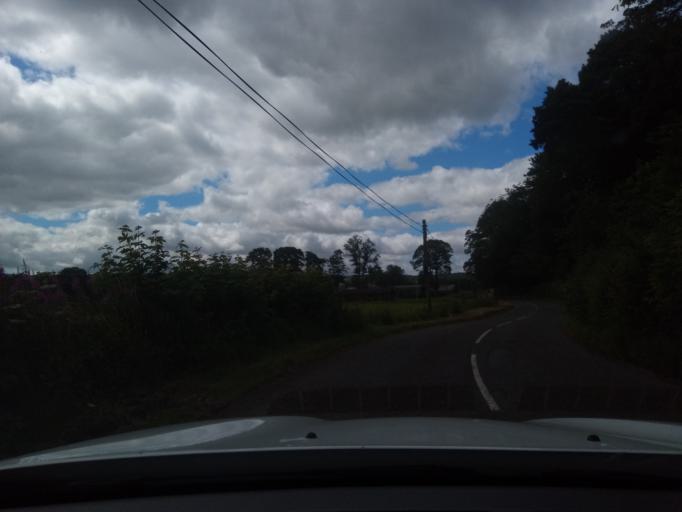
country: GB
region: Scotland
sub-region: The Scottish Borders
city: Selkirk
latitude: 55.5420
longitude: -2.8708
